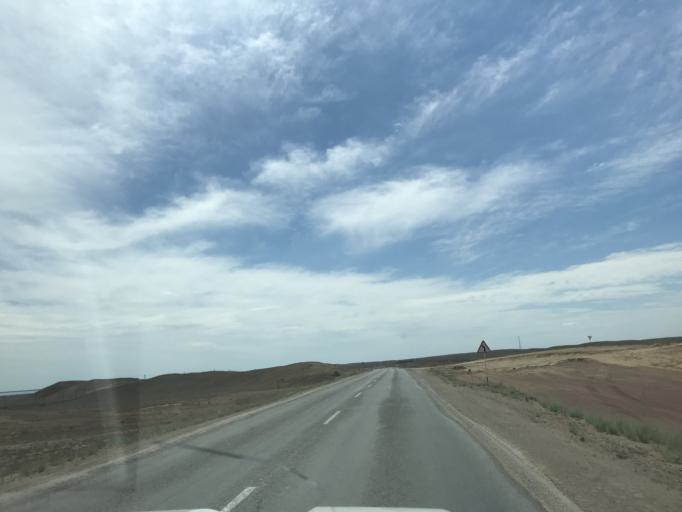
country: KZ
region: Almaty Oblysy
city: Ulken
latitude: 45.0802
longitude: 73.9727
